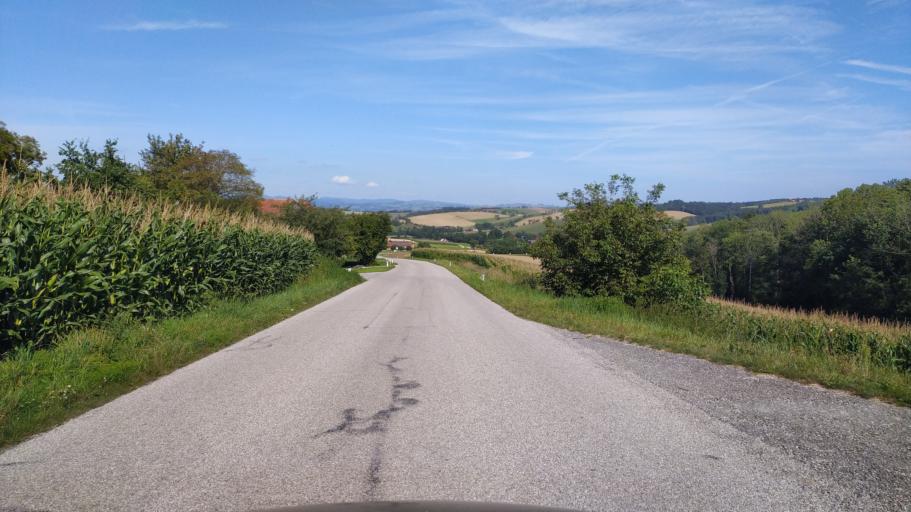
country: AT
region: Lower Austria
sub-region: Politischer Bezirk Amstetten
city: Strengberg
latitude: 48.1216
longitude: 14.6478
